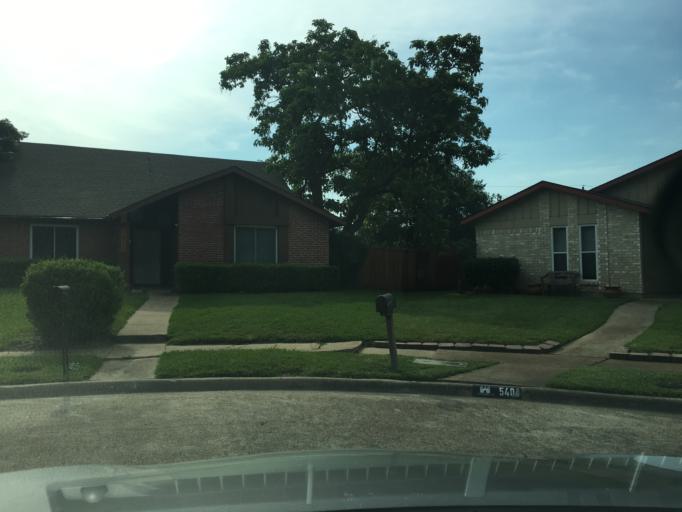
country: US
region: Texas
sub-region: Dallas County
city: Garland
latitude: 32.9650
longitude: -96.6706
